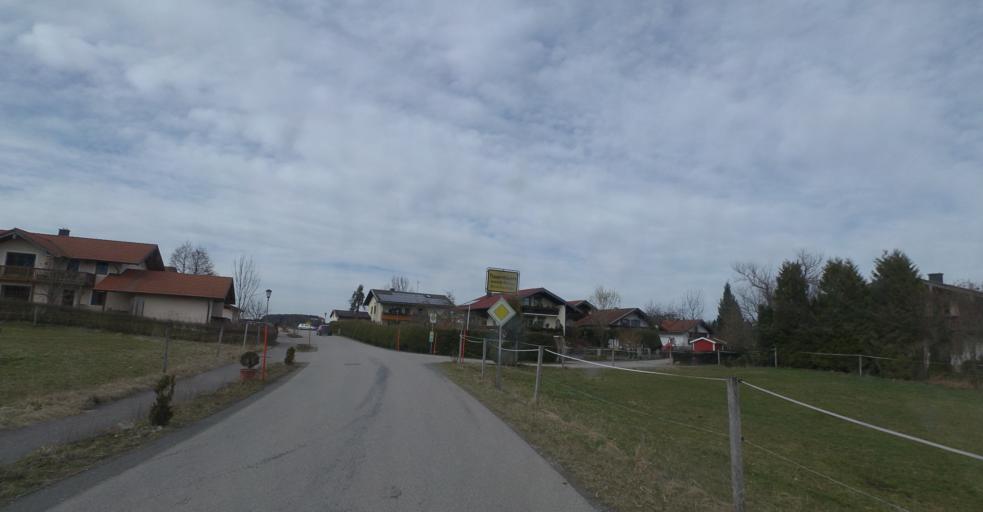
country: DE
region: Bavaria
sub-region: Upper Bavaria
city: Seeon-Seebruck
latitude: 47.9323
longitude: 12.5025
